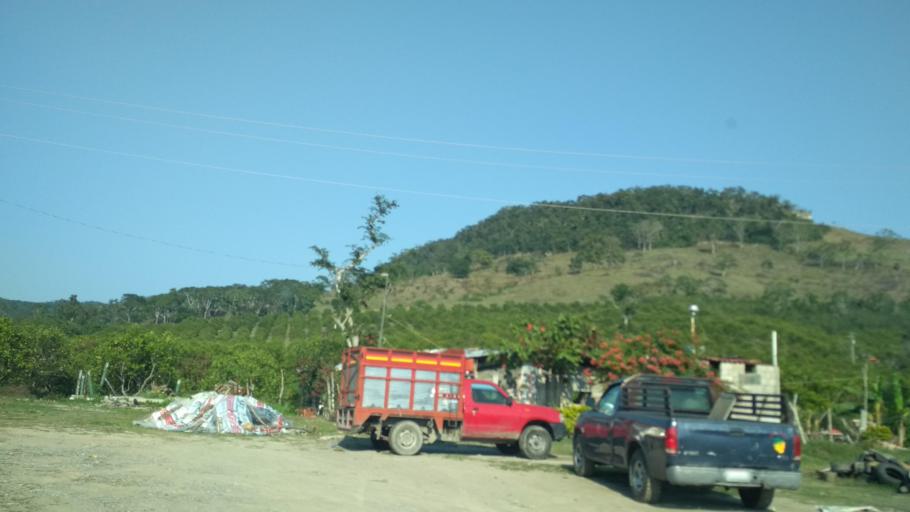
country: MM
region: Shan
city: Taunggyi
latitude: 20.4017
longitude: 97.3288
